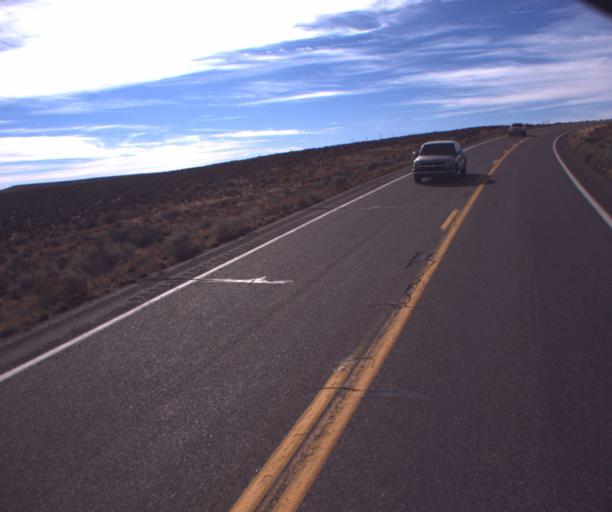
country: US
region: Arizona
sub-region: Coconino County
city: LeChee
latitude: 36.8147
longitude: -111.3062
